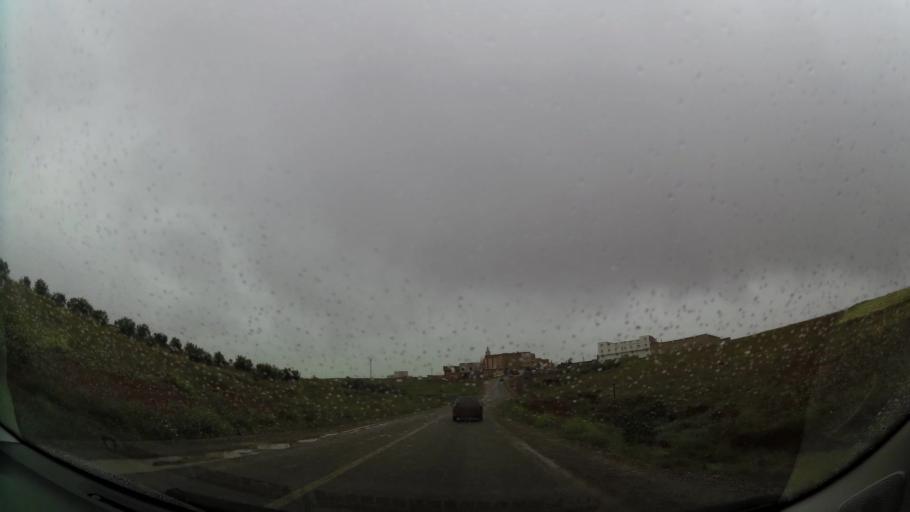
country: MA
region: Oriental
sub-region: Nador
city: Boudinar
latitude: 35.1270
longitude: -3.6288
